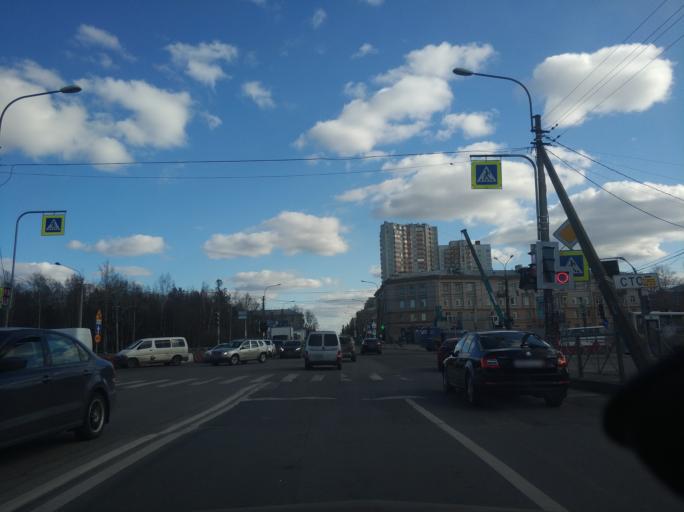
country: RU
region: St.-Petersburg
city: Krasnogvargeisky
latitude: 59.9623
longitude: 30.4882
